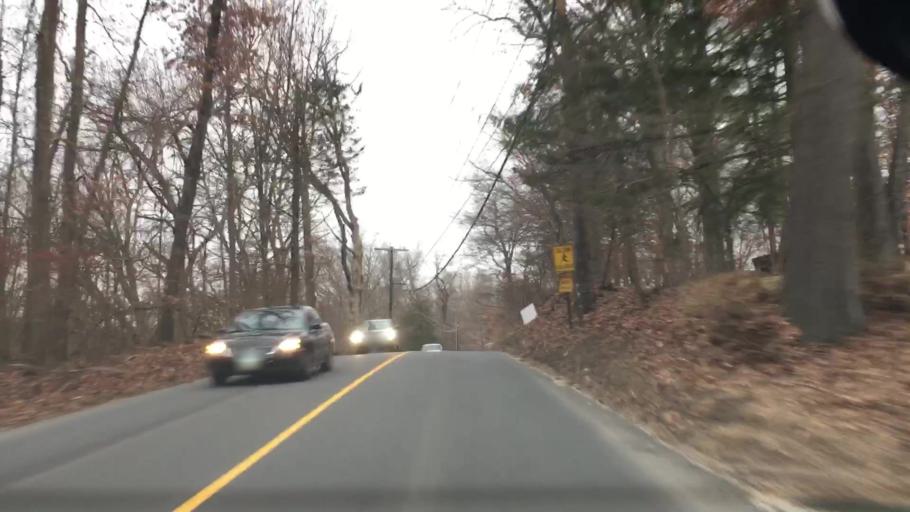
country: US
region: Connecticut
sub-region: Fairfield County
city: Bethel
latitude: 41.3942
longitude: -73.4011
